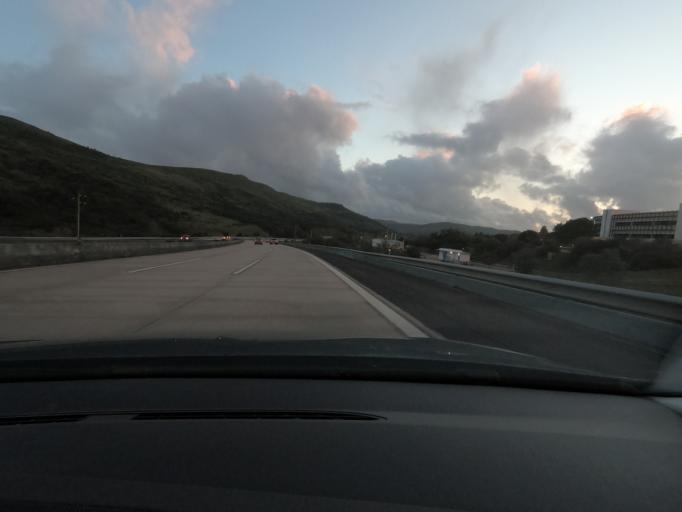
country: PT
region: Lisbon
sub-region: Loures
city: Bucelas
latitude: 38.9053
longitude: -9.0892
